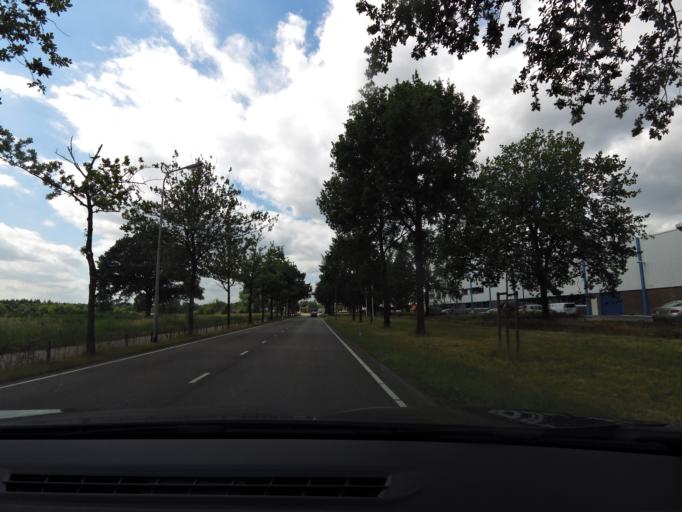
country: NL
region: North Brabant
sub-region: Gemeente Dongen
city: Dongen
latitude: 51.6158
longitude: 4.9224
